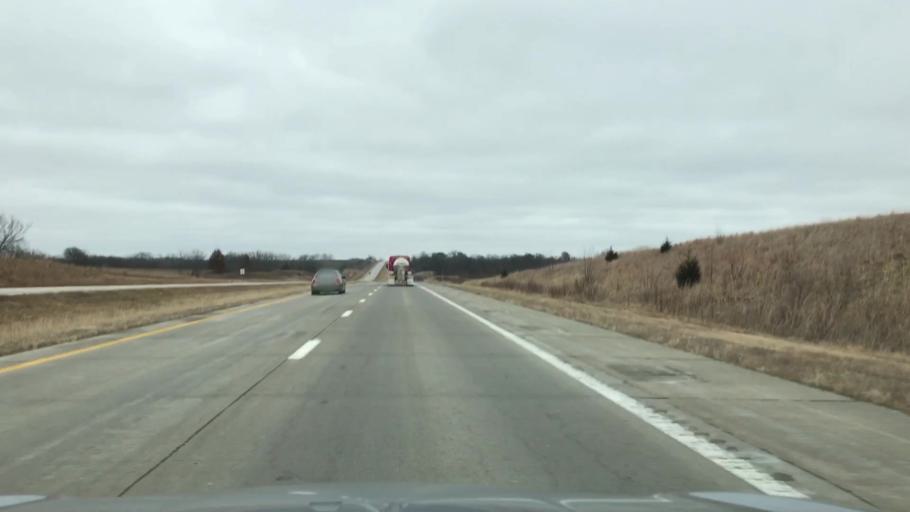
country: US
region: Missouri
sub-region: Caldwell County
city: Hamilton
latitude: 39.7348
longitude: -93.9487
